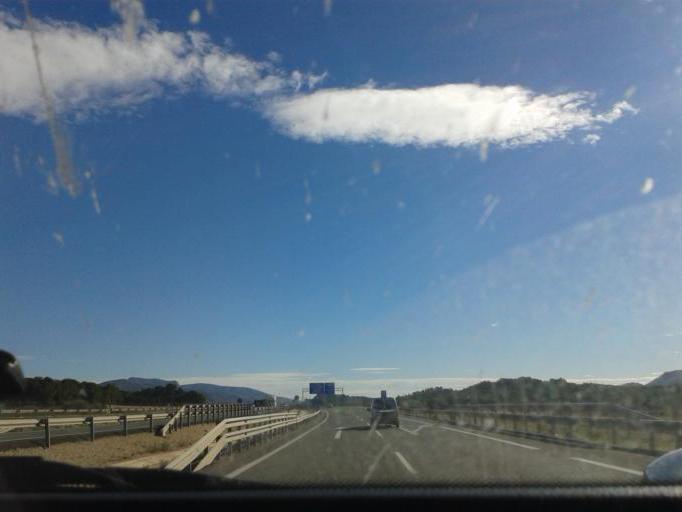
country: ES
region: Valencia
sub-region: Provincia de Alicante
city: Sax
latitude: 38.5659
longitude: -0.8346
